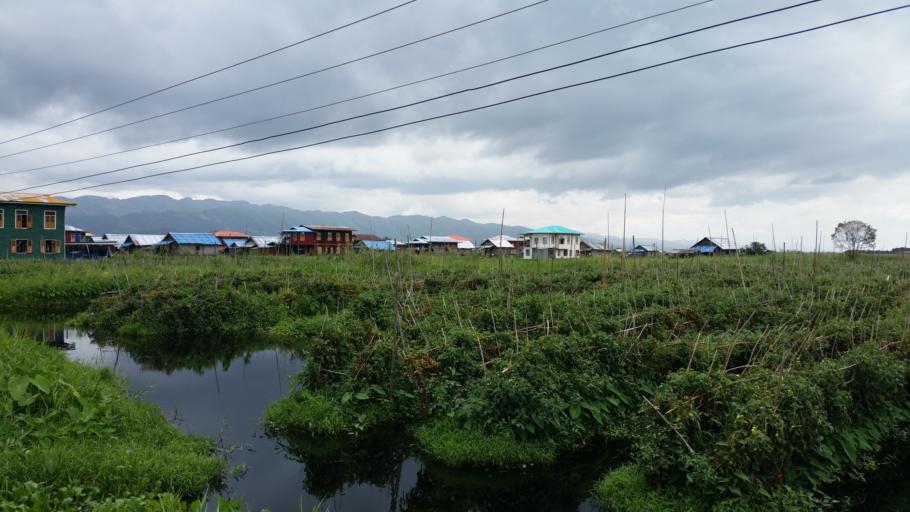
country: MM
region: Shan
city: Taunggyi
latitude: 20.5812
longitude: 96.9354
